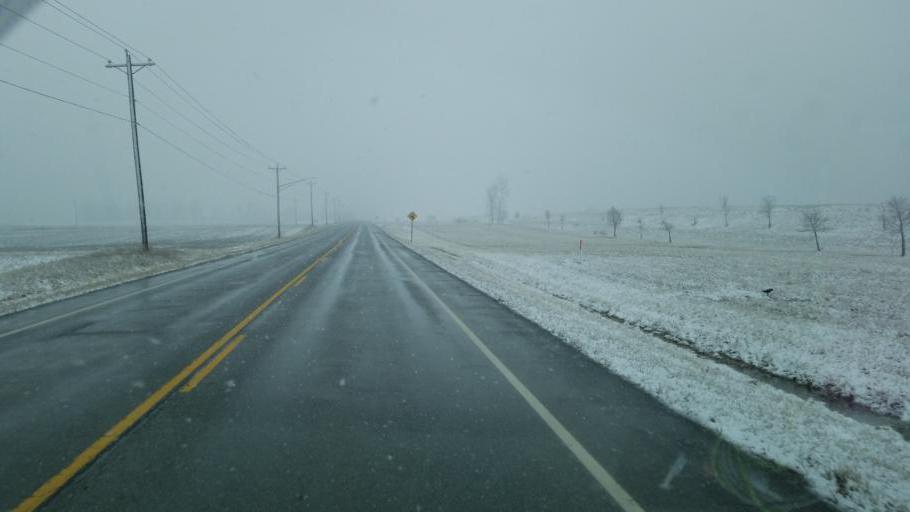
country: US
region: Ohio
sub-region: Champaign County
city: North Lewisburg
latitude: 40.2974
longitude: -83.5087
